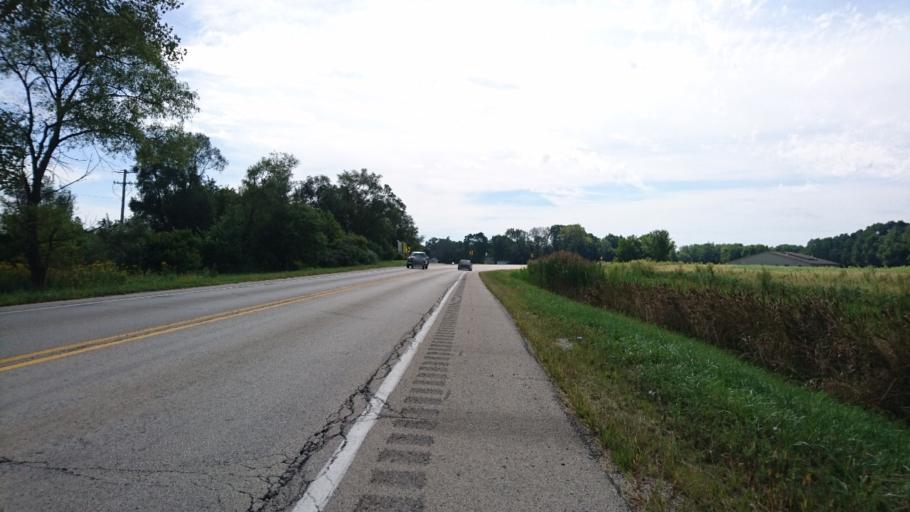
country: US
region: Illinois
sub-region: Will County
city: Wilmington
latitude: 41.3136
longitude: -88.1324
